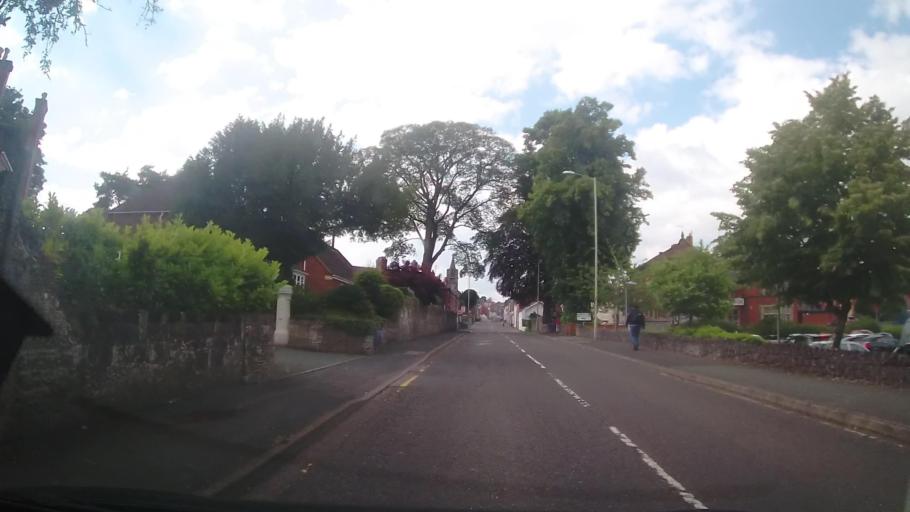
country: GB
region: England
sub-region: Shropshire
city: Oswestry
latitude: 52.8559
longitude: -3.0499
